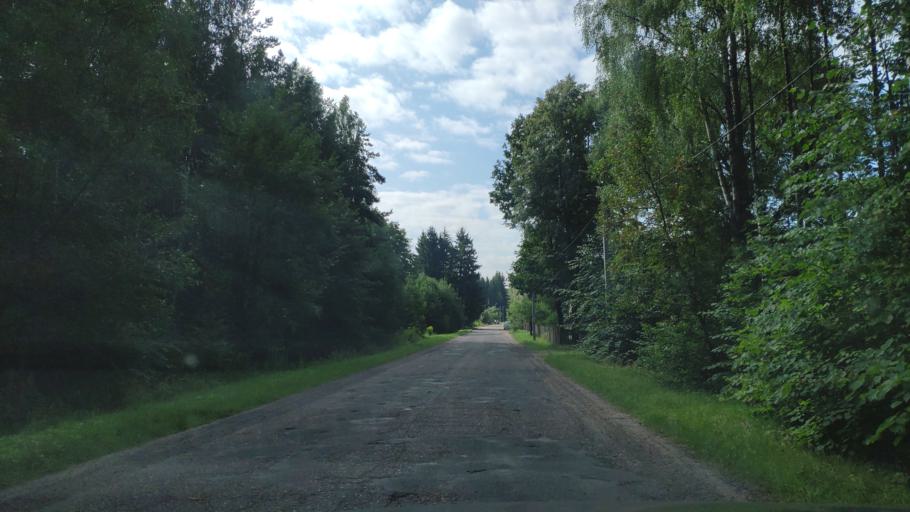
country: BY
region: Minsk
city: Zaslawye
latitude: 53.9795
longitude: 27.2897
